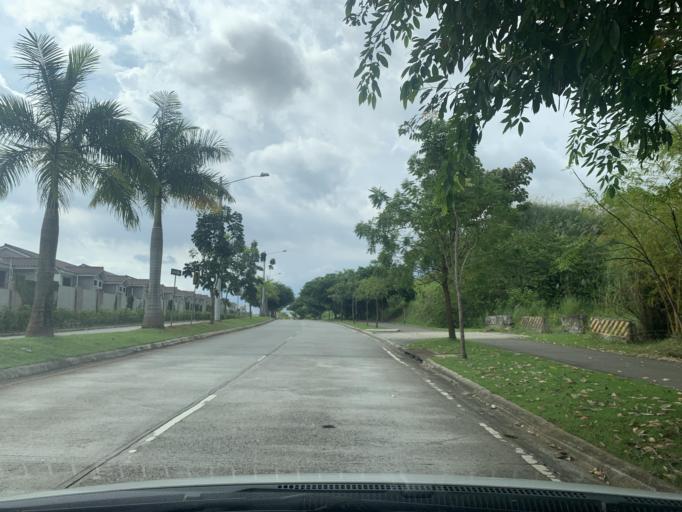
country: PA
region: Panama
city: San Miguelito
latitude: 9.0885
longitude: -79.4641
